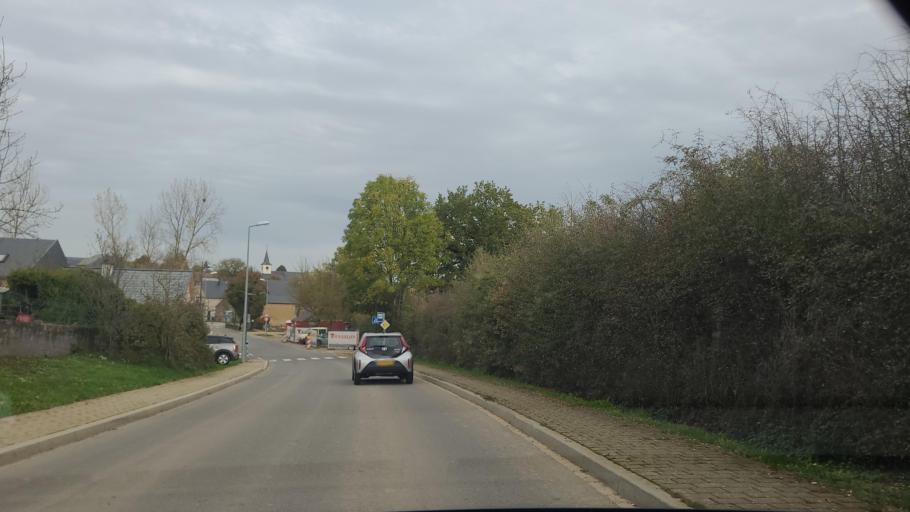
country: LU
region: Luxembourg
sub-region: Canton de Capellen
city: Dippach
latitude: 49.6126
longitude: 5.9904
